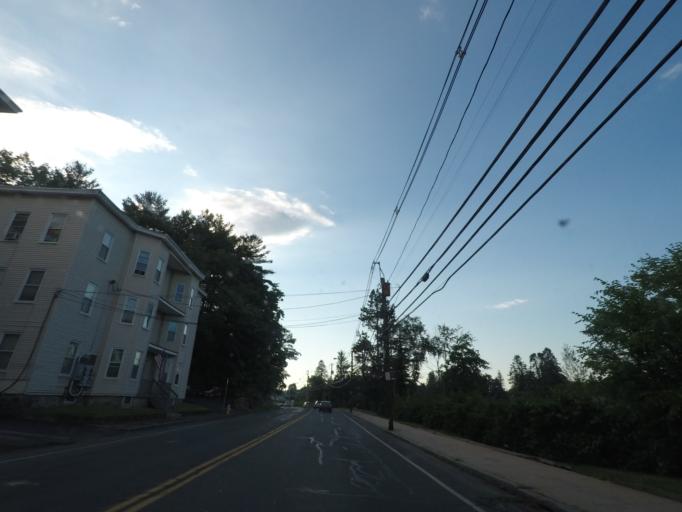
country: US
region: Massachusetts
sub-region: Worcester County
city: Southbridge
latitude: 42.0714
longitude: -72.0237
